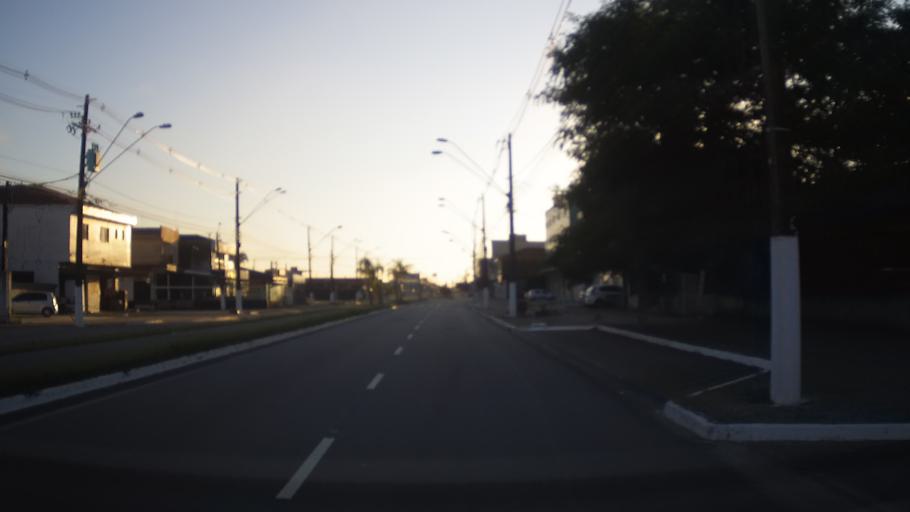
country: BR
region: Sao Paulo
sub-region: Praia Grande
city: Praia Grande
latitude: -24.0392
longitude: -46.5126
